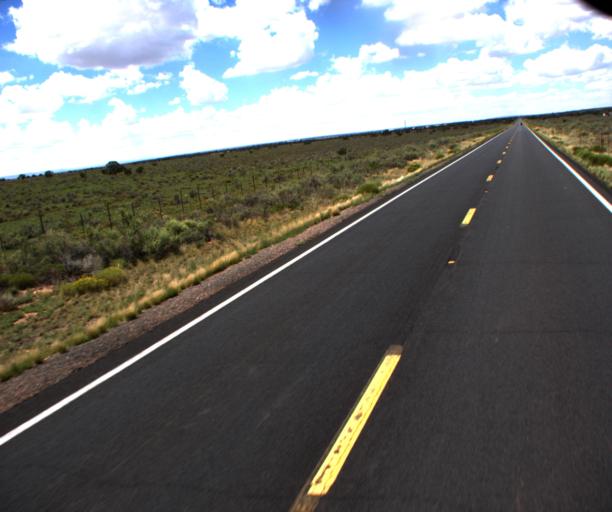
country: US
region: Arizona
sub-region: Coconino County
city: Williams
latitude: 35.6308
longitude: -112.1178
